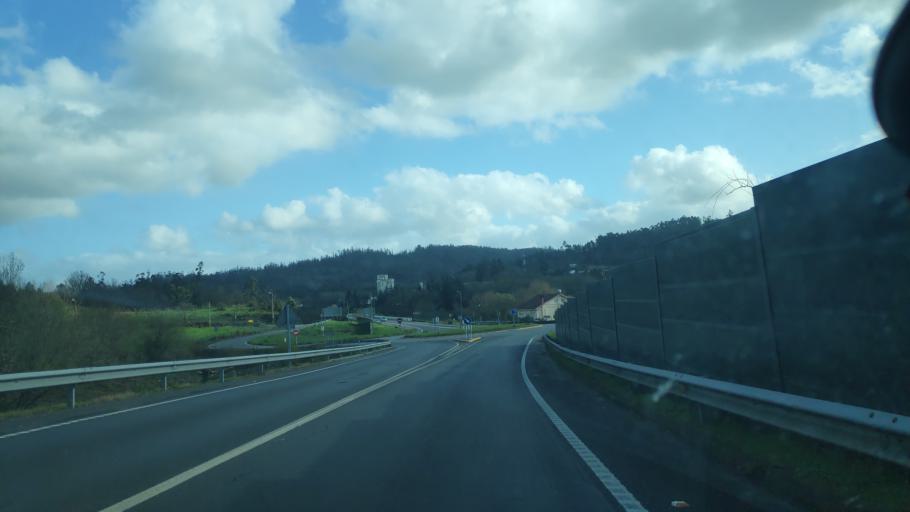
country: ES
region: Galicia
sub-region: Provincia da Coruna
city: Negreira
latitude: 42.9036
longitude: -8.7082
